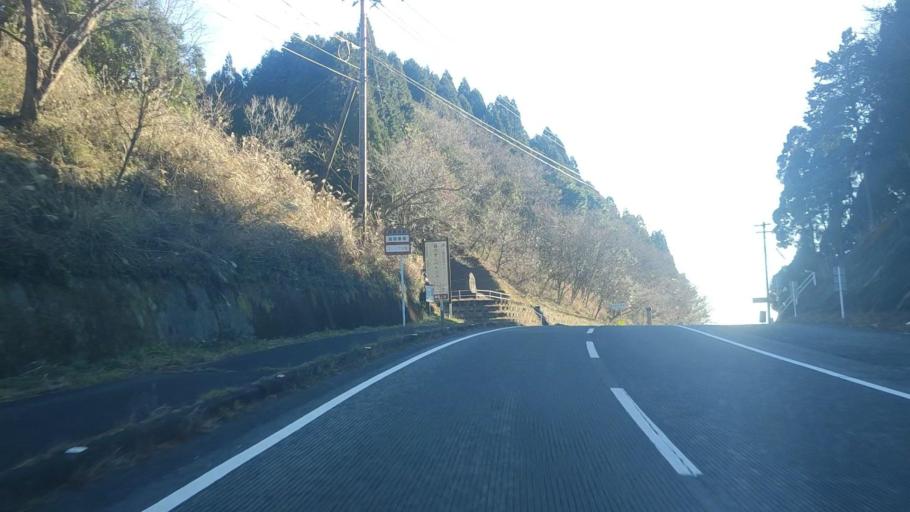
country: JP
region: Saga Prefecture
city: Kanzakimachi-kanzaki
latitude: 33.4044
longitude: 130.2729
